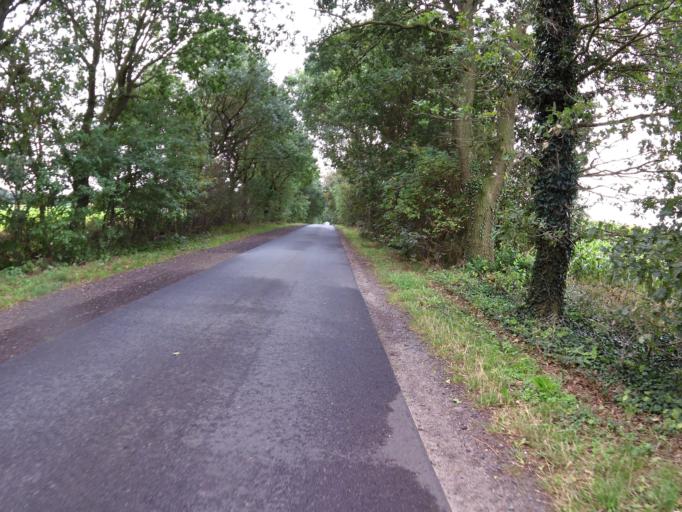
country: DE
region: Lower Saxony
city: Helvesiek
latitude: 53.2003
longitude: 9.4625
